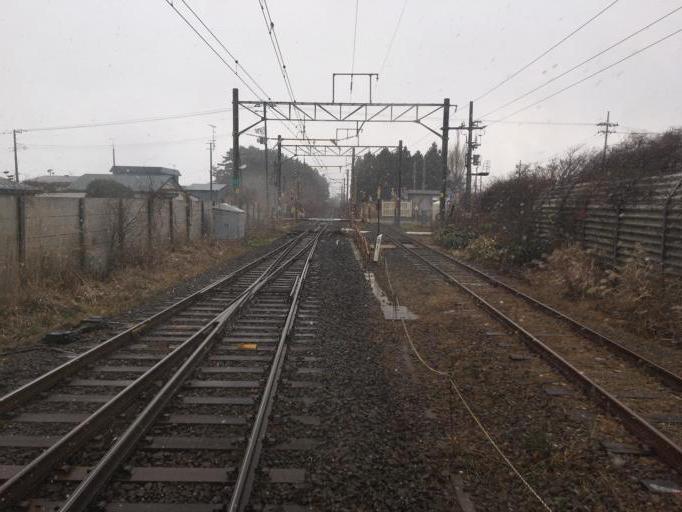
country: JP
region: Aomori
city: Aomori Shi
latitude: 40.9869
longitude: 140.6526
